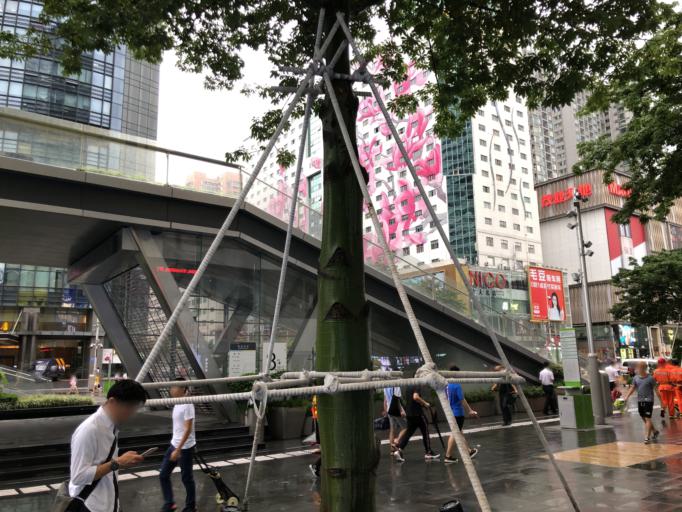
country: CN
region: Guangdong
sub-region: Shenzhen
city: Shenzhen
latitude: 22.5465
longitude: 114.0820
